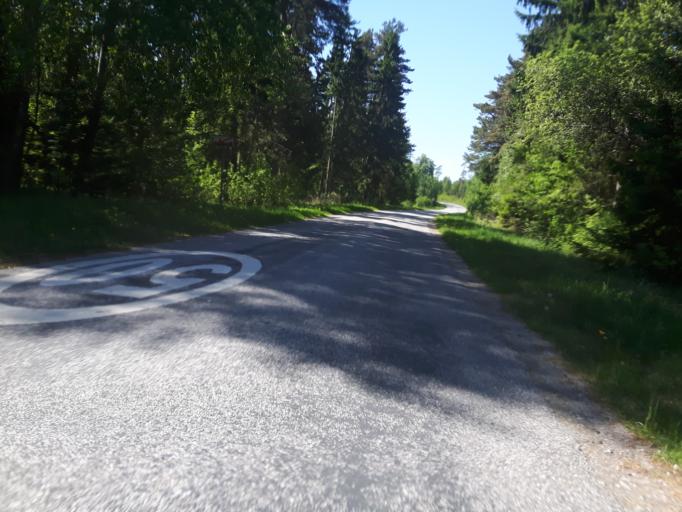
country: EE
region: Laeaene-Virumaa
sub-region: Haljala vald
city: Haljala
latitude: 59.5506
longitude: 26.3723
